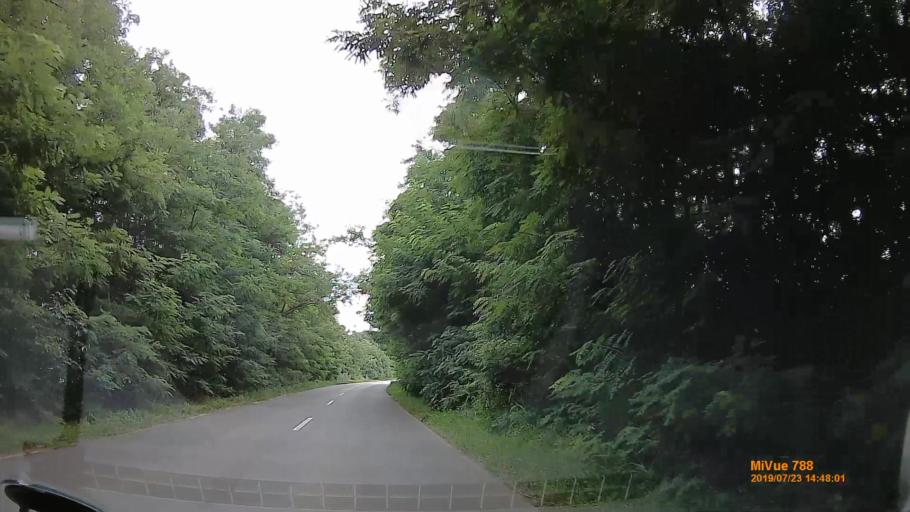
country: HU
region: Szabolcs-Szatmar-Bereg
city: Nyiregyhaza
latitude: 47.9068
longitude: 21.6724
